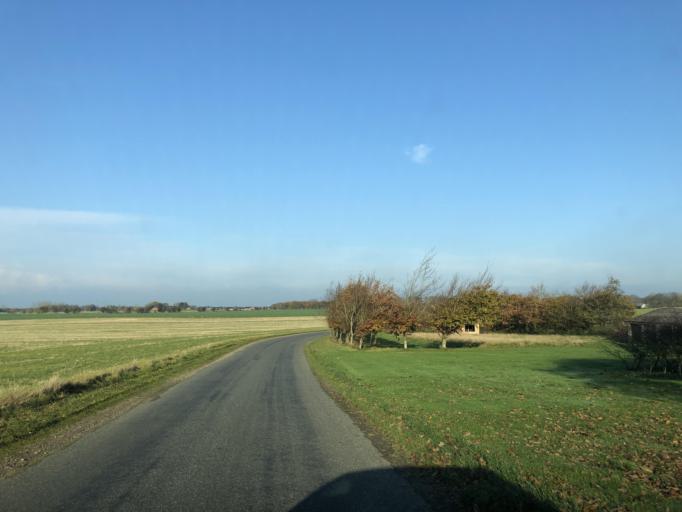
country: DK
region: Central Jutland
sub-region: Holstebro Kommune
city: Vinderup
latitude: 56.3983
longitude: 8.7466
